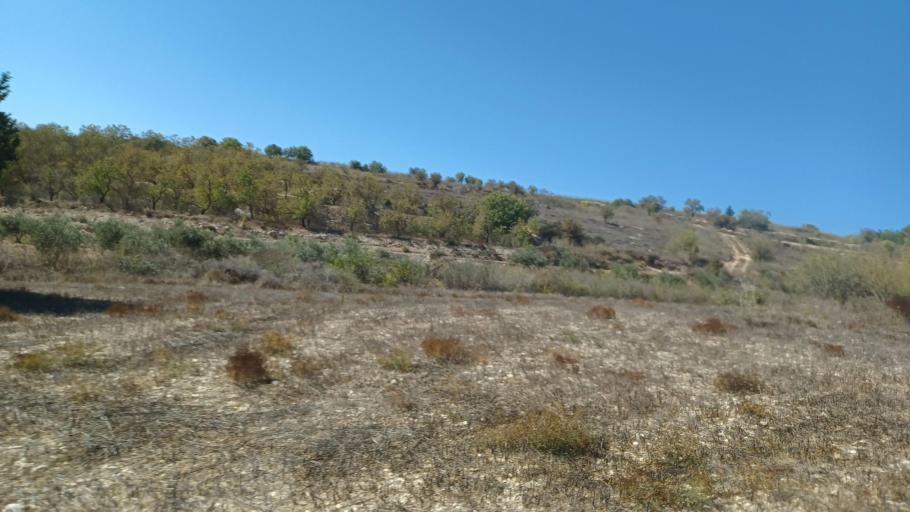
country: CY
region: Pafos
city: Mesogi
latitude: 34.8152
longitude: 32.4883
